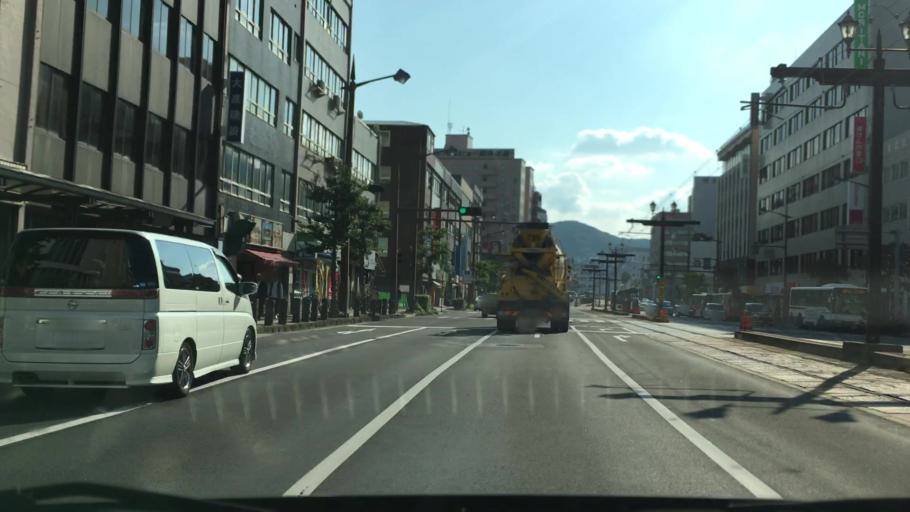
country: JP
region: Nagasaki
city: Nagasaki-shi
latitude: 32.7473
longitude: 129.8725
